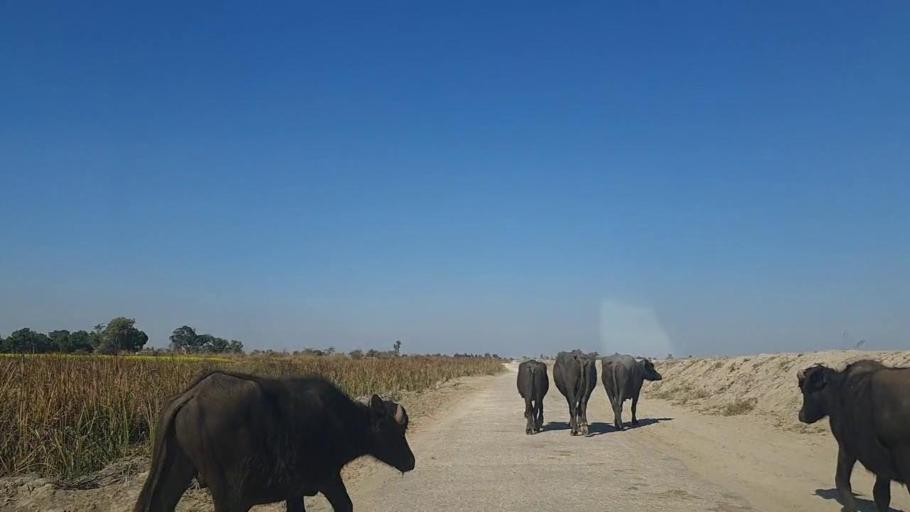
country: PK
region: Sindh
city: Sanghar
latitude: 26.2122
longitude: 68.9293
